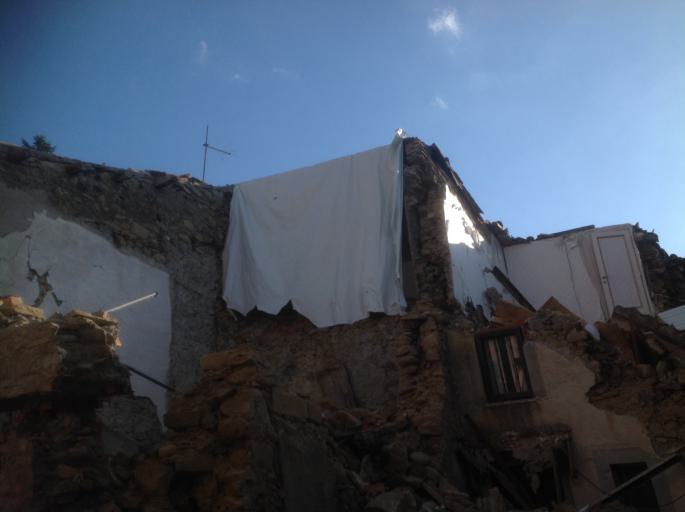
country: IT
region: Latium
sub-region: Provincia di Rieti
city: Amatrice
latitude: 42.6223
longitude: 13.3399
